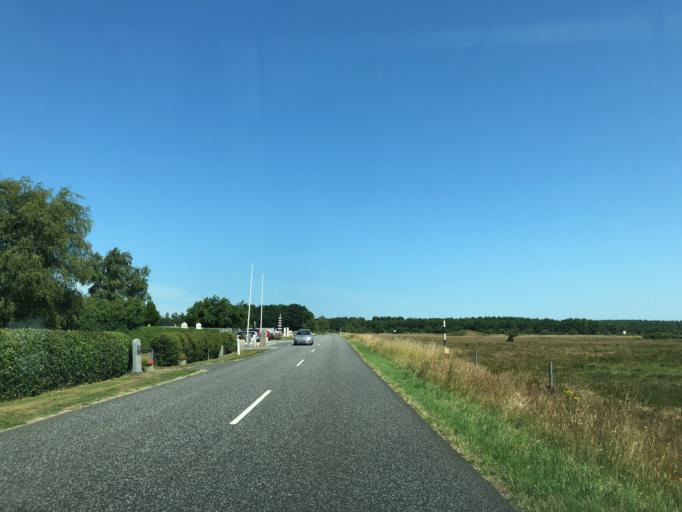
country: DK
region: Central Jutland
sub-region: Skive Kommune
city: Skive
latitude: 56.5278
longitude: 9.0347
